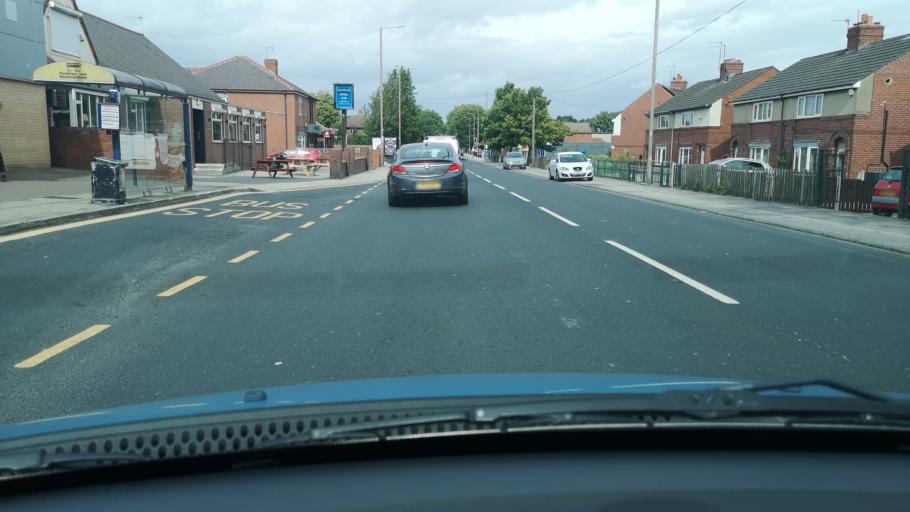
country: GB
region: England
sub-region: Barnsley
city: Cudworth
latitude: 53.5585
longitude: -1.4376
